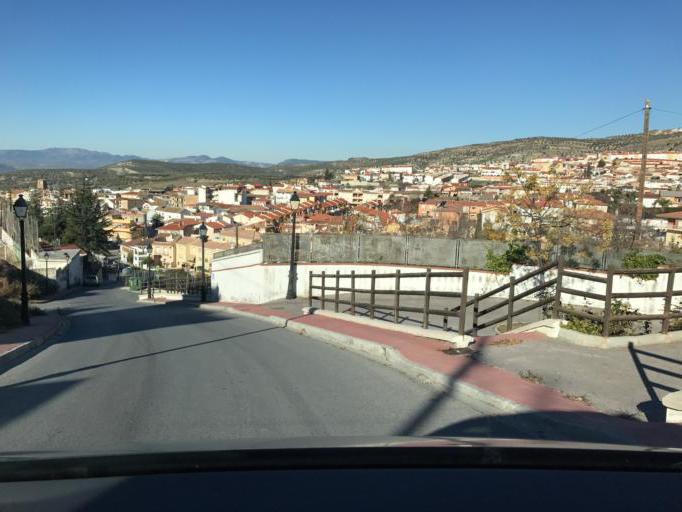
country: ES
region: Andalusia
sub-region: Provincia de Granada
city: Alfacar
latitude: 37.2355
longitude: -3.5625
